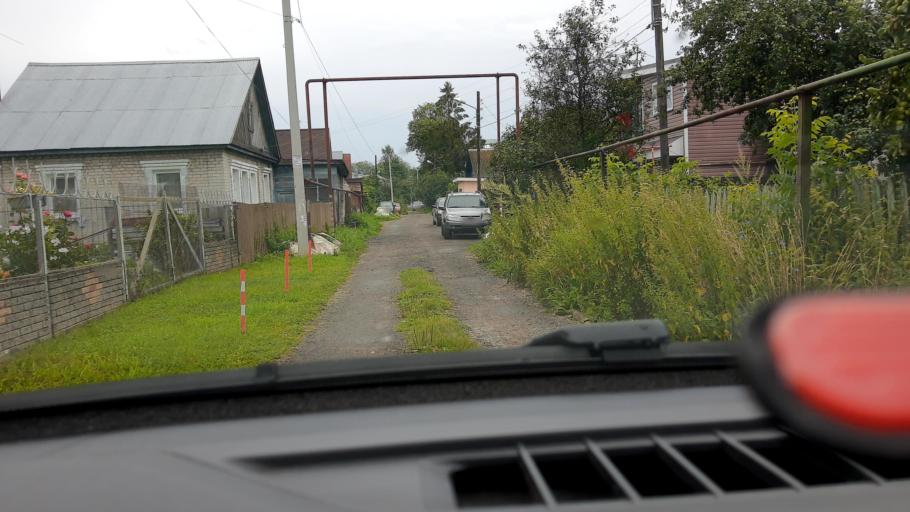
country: RU
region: Nizjnij Novgorod
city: Gorbatovka
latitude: 56.3750
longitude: 43.8266
